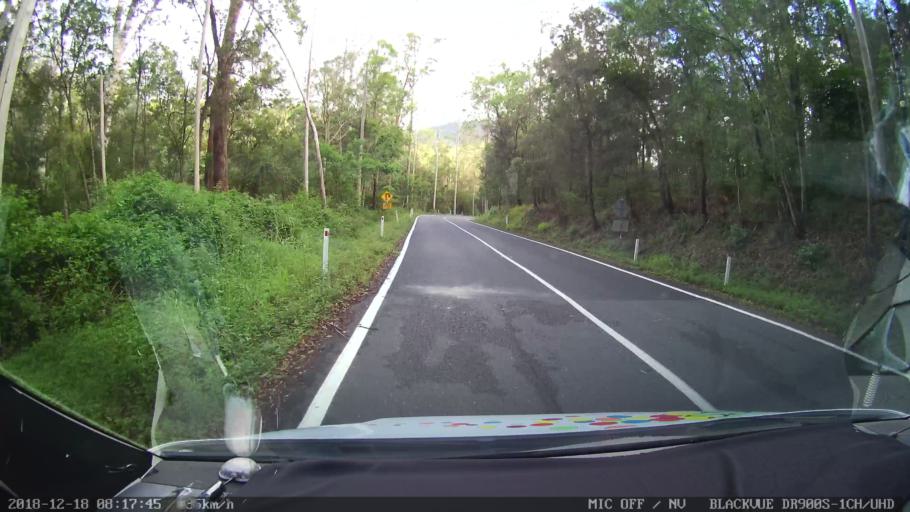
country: AU
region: New South Wales
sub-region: Kyogle
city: Kyogle
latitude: -28.3370
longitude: 152.7033
